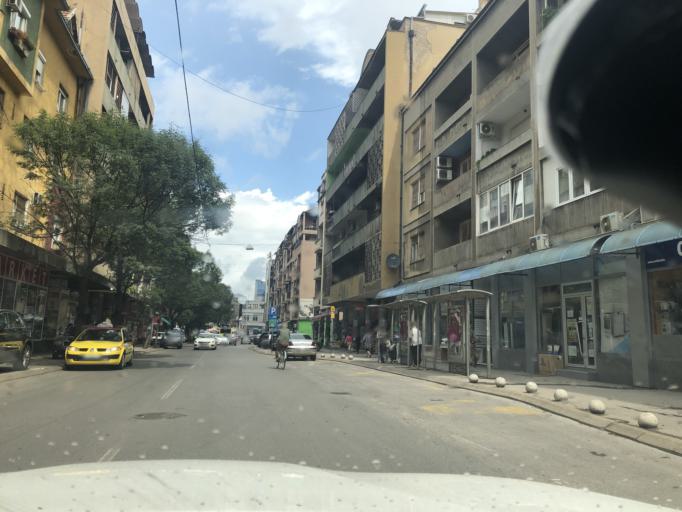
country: RS
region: Central Serbia
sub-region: Nisavski Okrug
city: Nis
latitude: 43.3153
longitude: 21.8946
